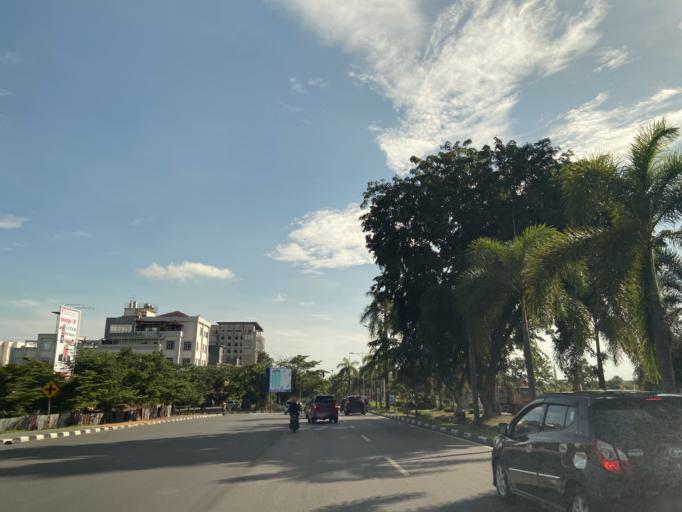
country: SG
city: Singapore
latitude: 1.1266
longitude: 104.0524
